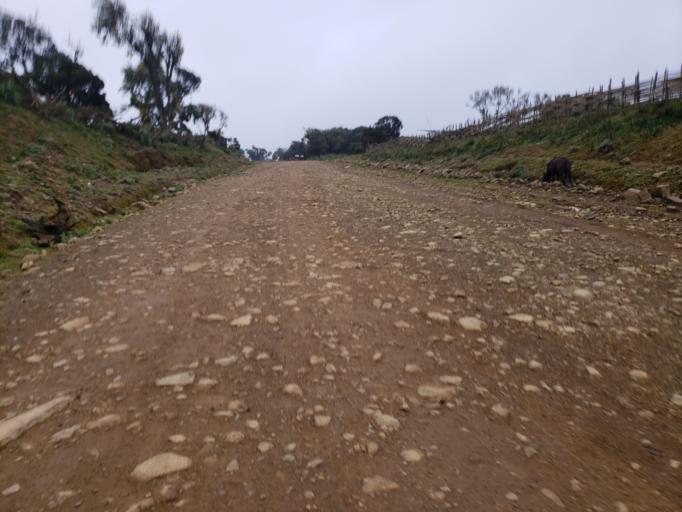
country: ET
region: Oromiya
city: Dodola
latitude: 6.7257
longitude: 39.4232
